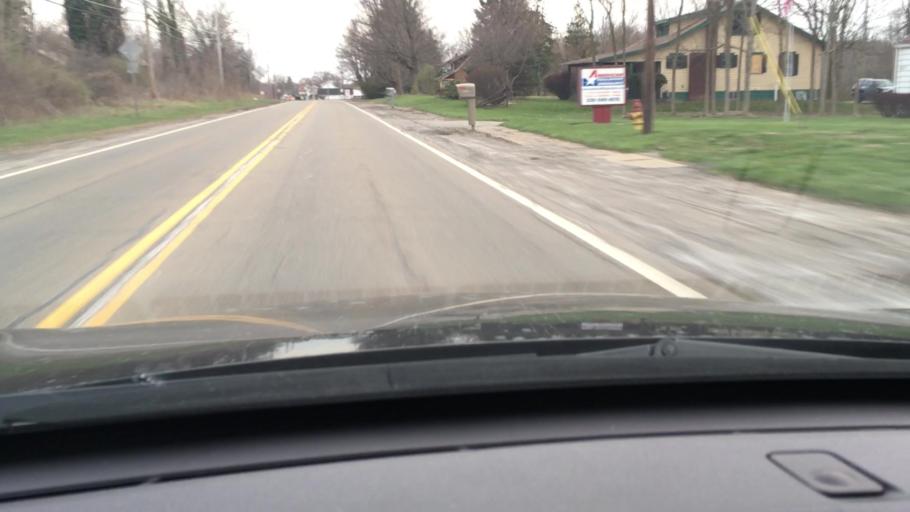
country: US
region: Ohio
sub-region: Mahoning County
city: Boardman
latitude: 40.9569
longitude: -80.6596
